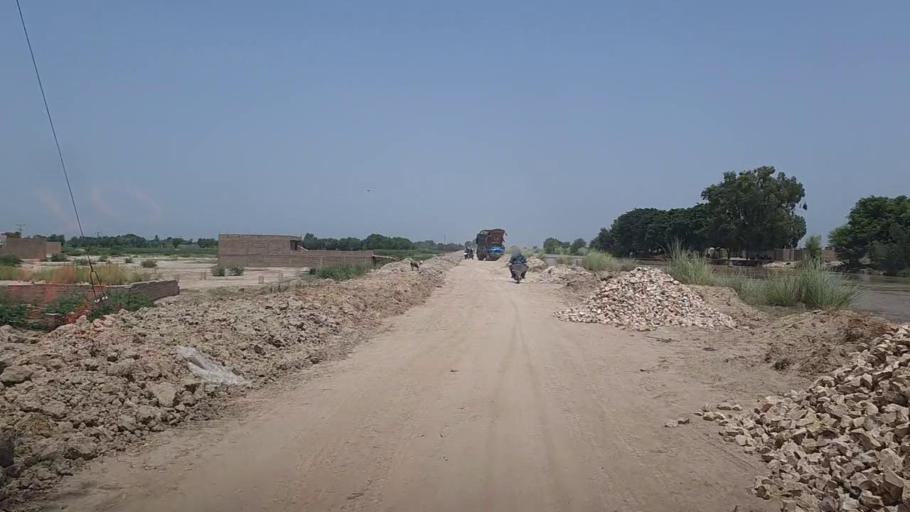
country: PK
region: Sindh
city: Pad Idan
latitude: 26.7840
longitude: 68.2780
